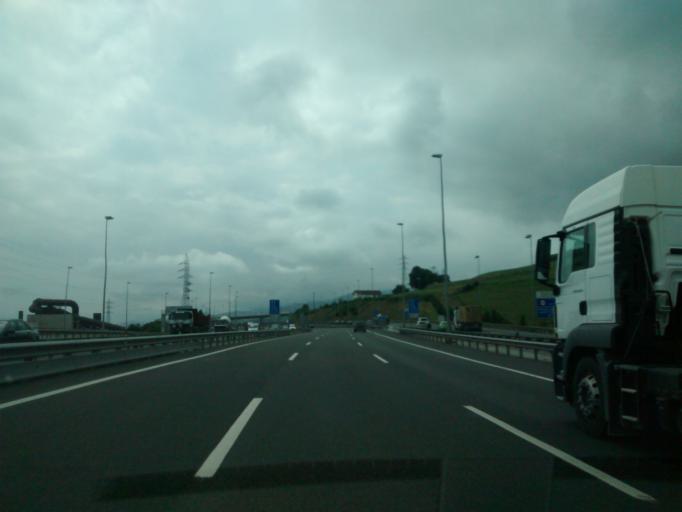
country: ES
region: Basque Country
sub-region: Bizkaia
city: Portugalete
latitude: 43.3090
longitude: -3.0291
